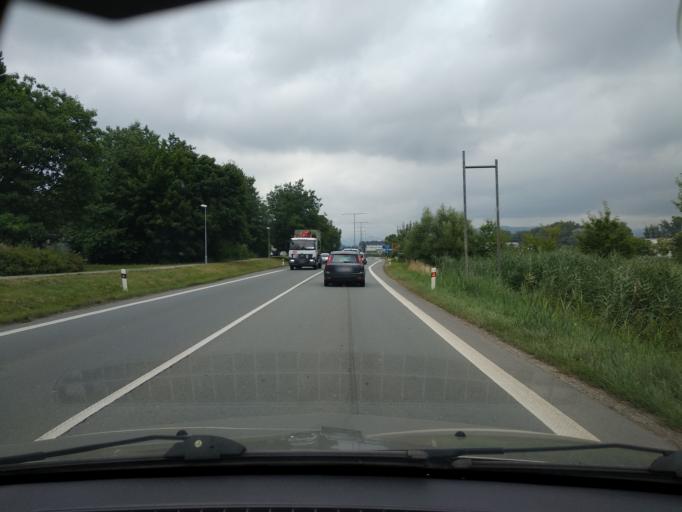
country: CZ
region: Olomoucky
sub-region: Okres Sumperk
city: Sumperk
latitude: 49.9507
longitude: 16.9576
